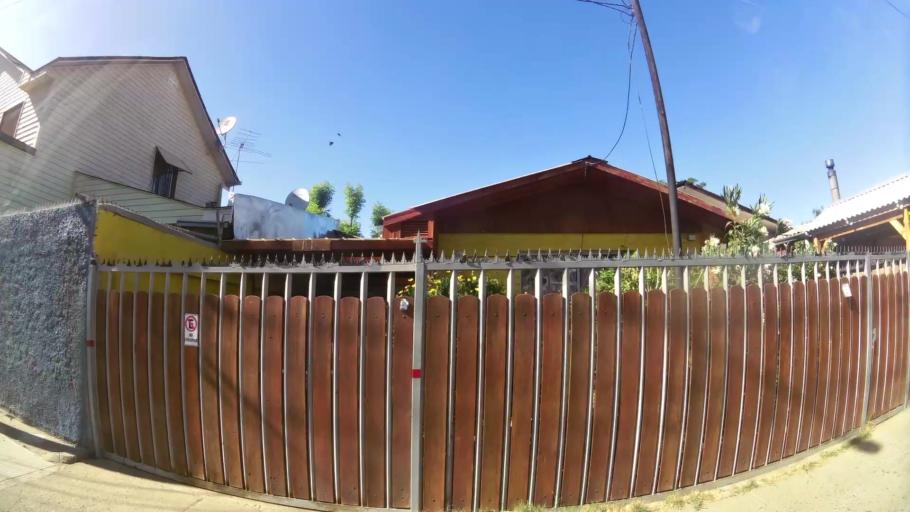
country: CL
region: Santiago Metropolitan
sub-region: Provincia de Chacabuco
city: Lampa
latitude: -33.4057
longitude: -71.1281
